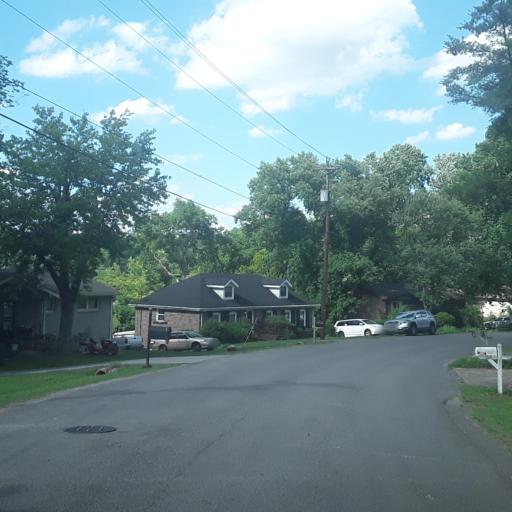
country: US
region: Tennessee
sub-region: Davidson County
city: Lakewood
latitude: 36.1934
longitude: -86.6307
